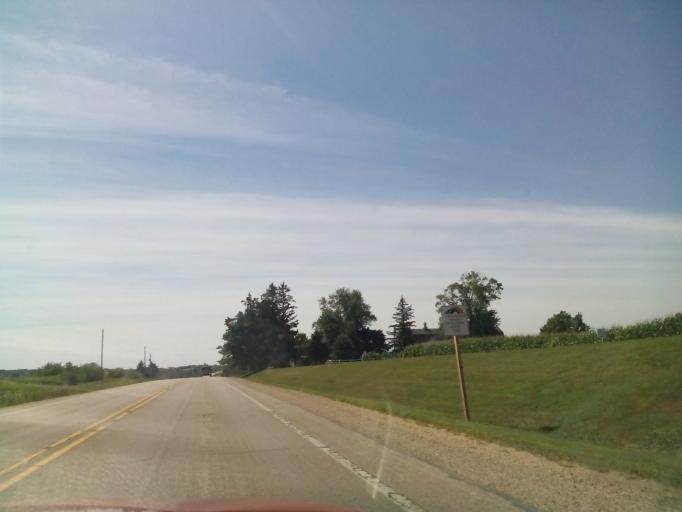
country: US
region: Wisconsin
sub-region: Green County
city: Monroe
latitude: 42.6462
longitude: -89.6316
